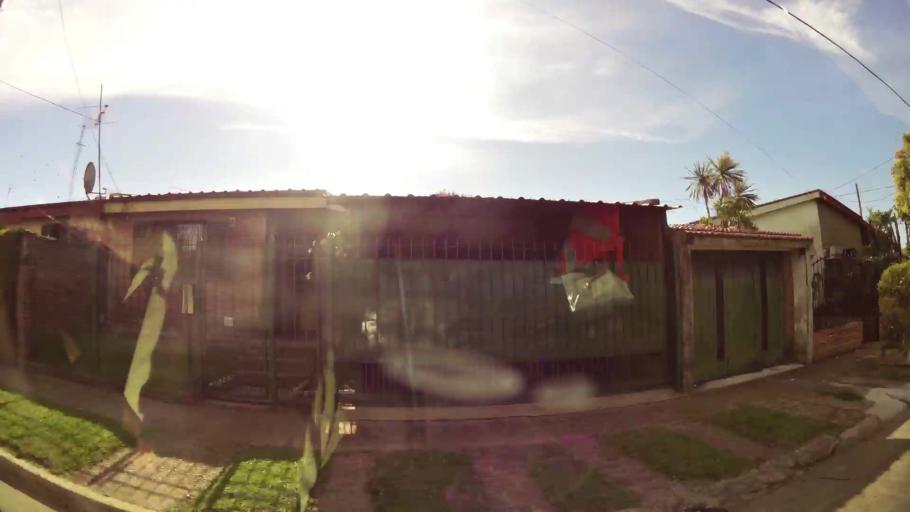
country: AR
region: Buenos Aires
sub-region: Partido de Almirante Brown
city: Adrogue
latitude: -34.8187
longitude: -58.3497
